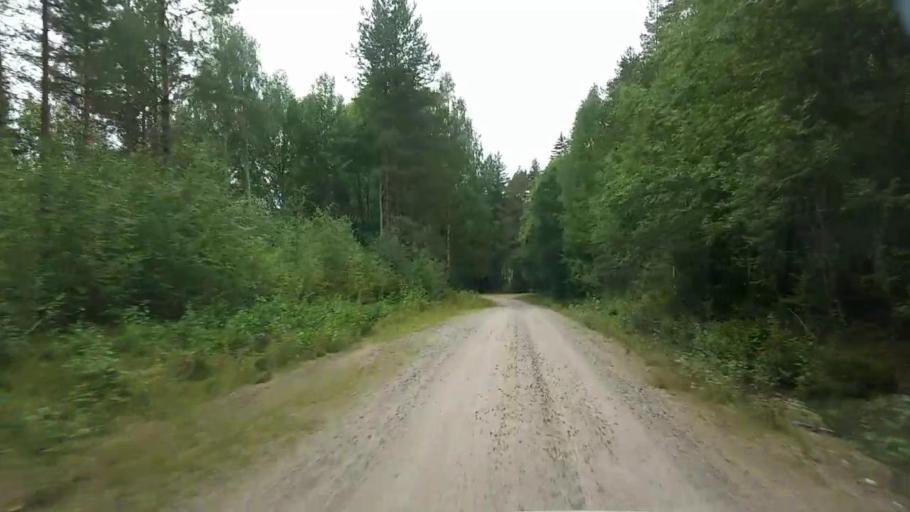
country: SE
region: Gaevleborg
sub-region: Ljusdals Kommun
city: Farila
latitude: 61.8120
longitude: 15.8662
